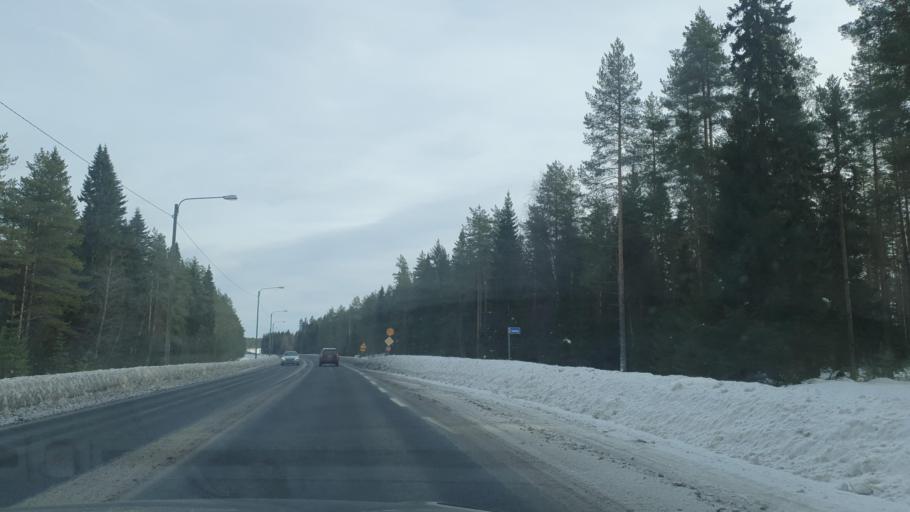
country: FI
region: Northern Ostrobothnia
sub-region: Oulu
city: Tyrnaevae
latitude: 64.9341
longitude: 25.7167
